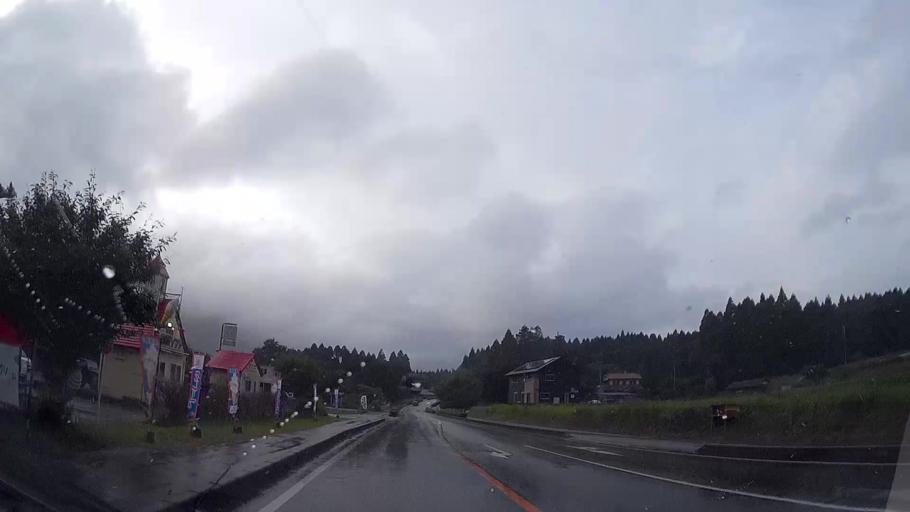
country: JP
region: Kumamoto
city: Aso
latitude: 32.8607
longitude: 131.0032
